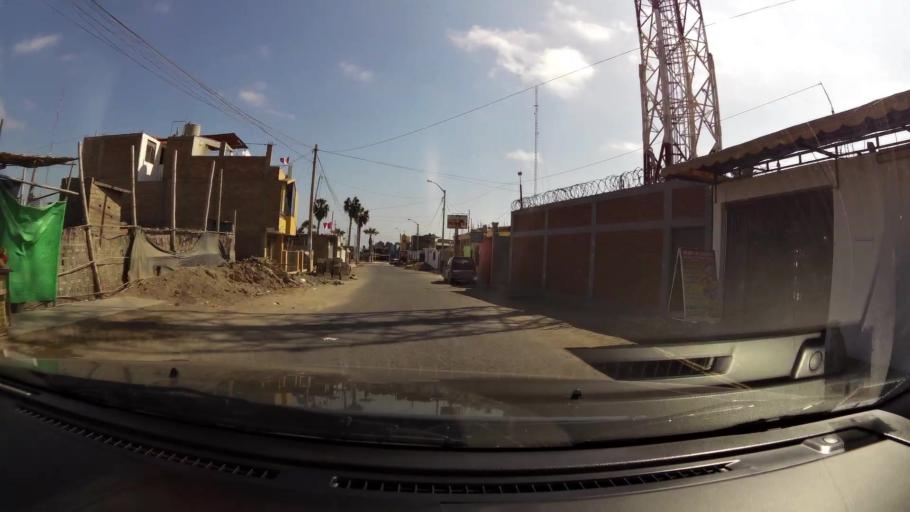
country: PE
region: Ica
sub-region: Provincia de Chincha
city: Sunampe
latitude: -13.4267
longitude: -76.1632
